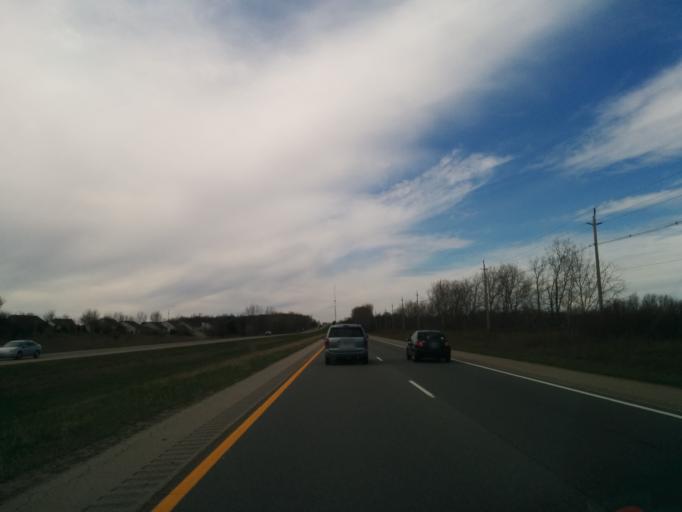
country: US
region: Michigan
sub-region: Ottawa County
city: Zeeland
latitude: 42.7968
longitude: -86.0001
